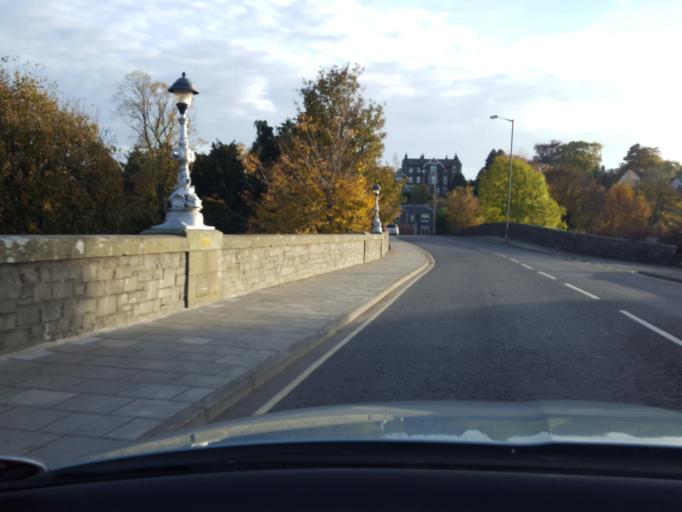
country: GB
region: Scotland
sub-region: The Scottish Borders
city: Peebles
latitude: 55.6505
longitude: -3.1926
